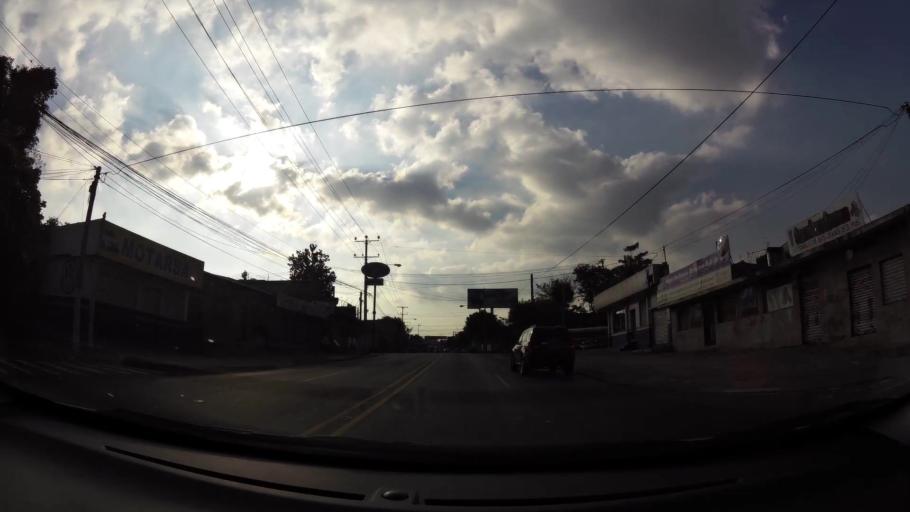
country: SV
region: San Salvador
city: San Salvador
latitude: 13.6917
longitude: -89.2138
